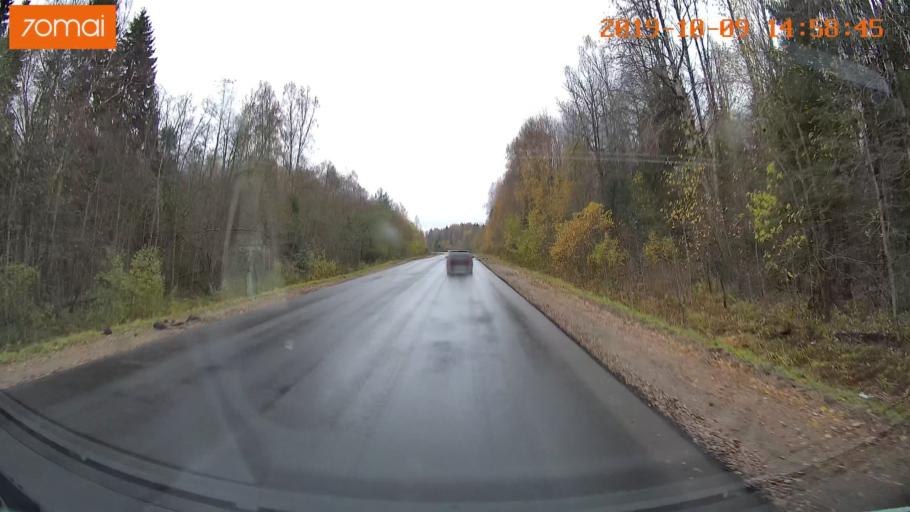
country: RU
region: Kostroma
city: Chistyye Bory
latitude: 58.3246
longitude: 41.6578
